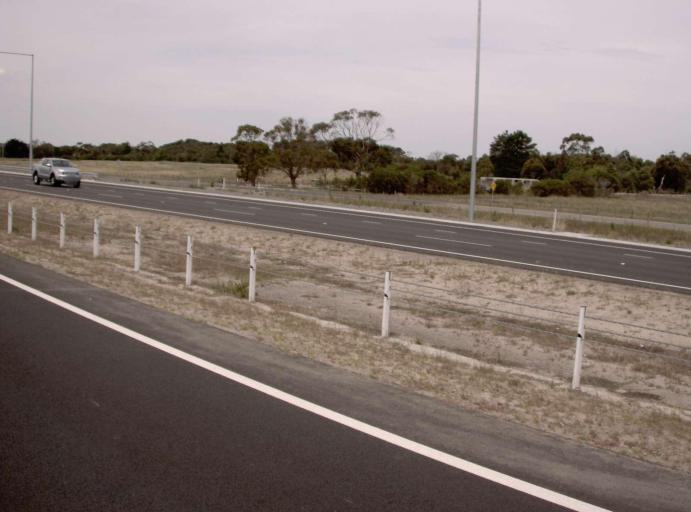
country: AU
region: Victoria
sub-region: Mornington Peninsula
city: Baxter
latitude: -38.1993
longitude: 145.1441
